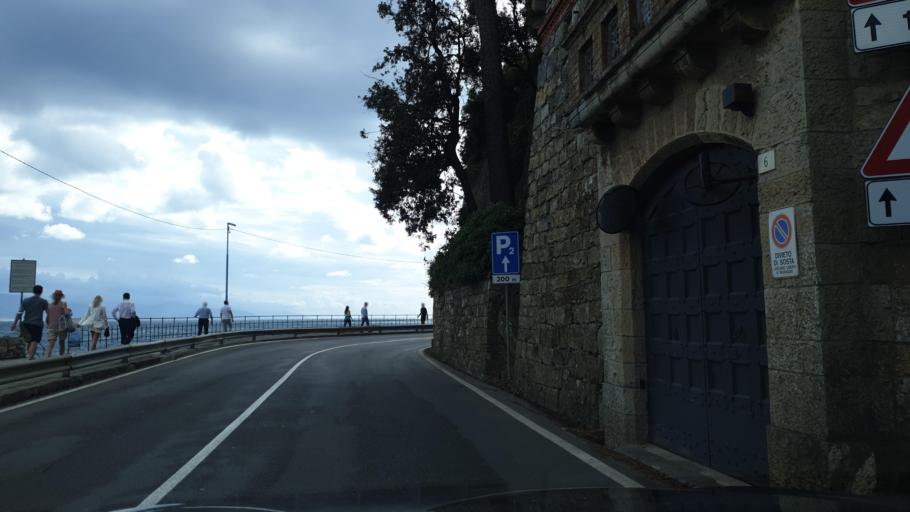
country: IT
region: Liguria
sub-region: Provincia di Genova
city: Santa Margherita Ligure
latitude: 44.3253
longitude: 9.2158
